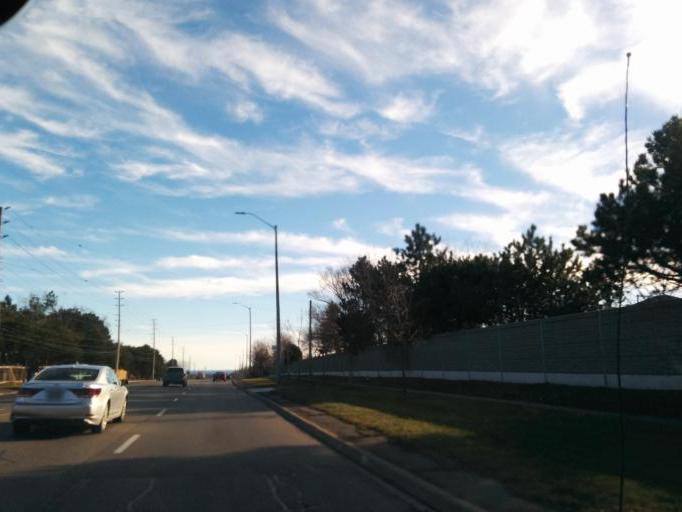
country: CA
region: Ontario
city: Oakville
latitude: 43.5047
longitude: -79.6570
